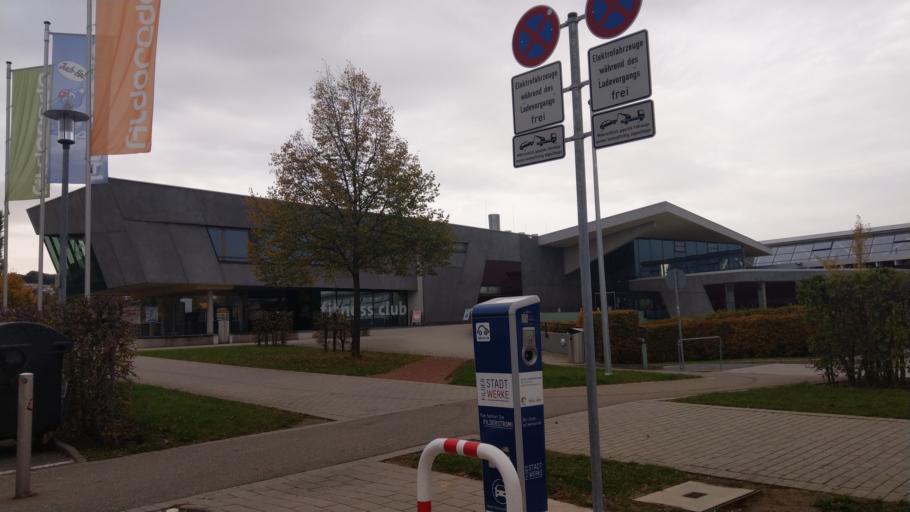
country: DE
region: Baden-Wuerttemberg
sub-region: Regierungsbezirk Stuttgart
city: Filderstadt
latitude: 48.6515
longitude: 9.2078
